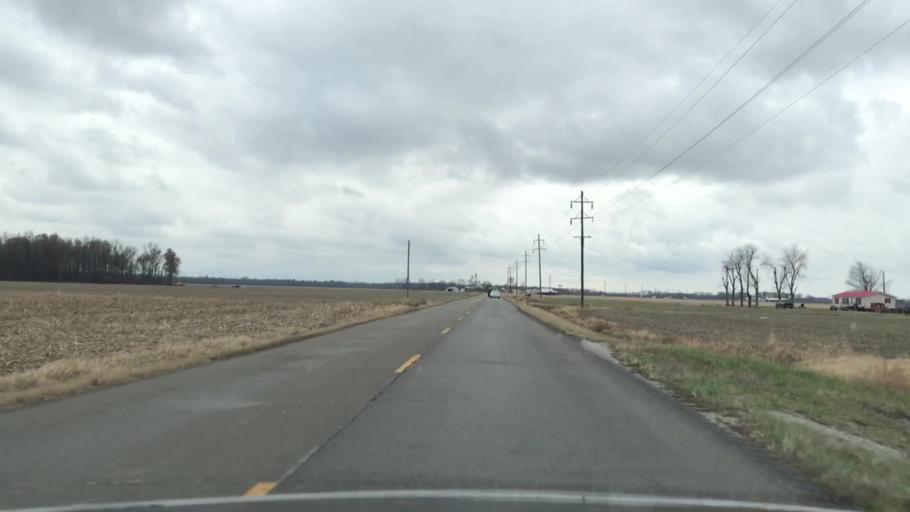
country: US
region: Kentucky
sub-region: McLean County
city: Calhoun
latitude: 37.5321
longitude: -87.3219
